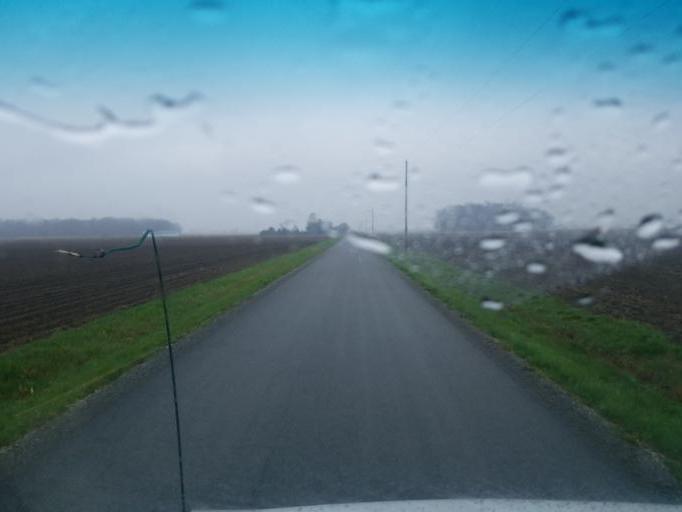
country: US
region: Ohio
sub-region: Wyandot County
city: Carey
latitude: 40.9923
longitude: -83.3543
